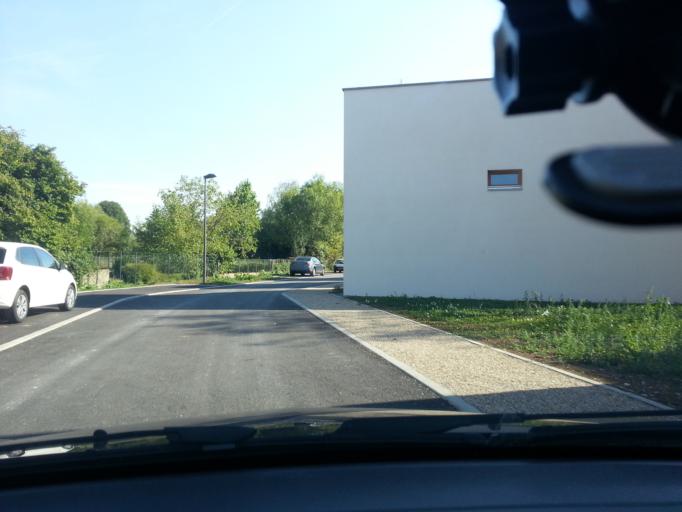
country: FR
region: Bourgogne
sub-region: Departement de Saone-et-Loire
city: Chatenoy-le-Royal
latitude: 46.7975
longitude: 4.8139
